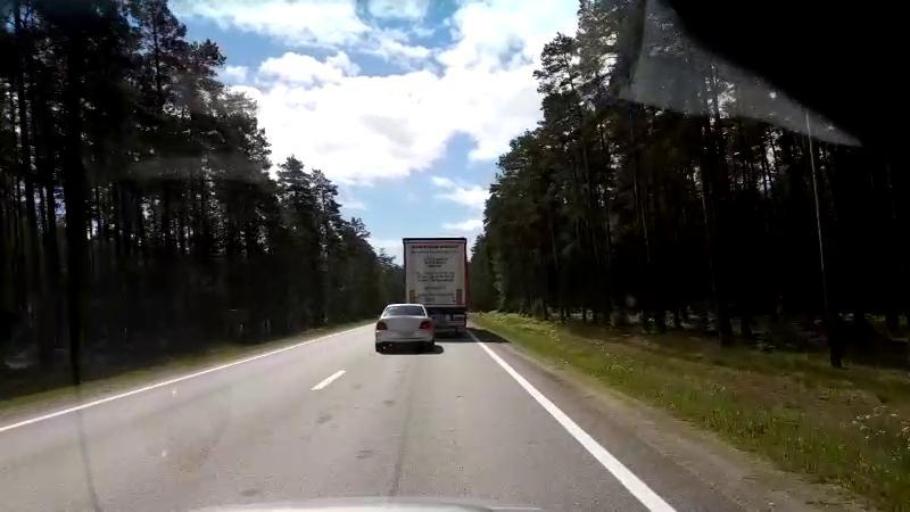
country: LV
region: Salacgrivas
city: Salacgriva
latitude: 57.5582
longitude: 24.4336
